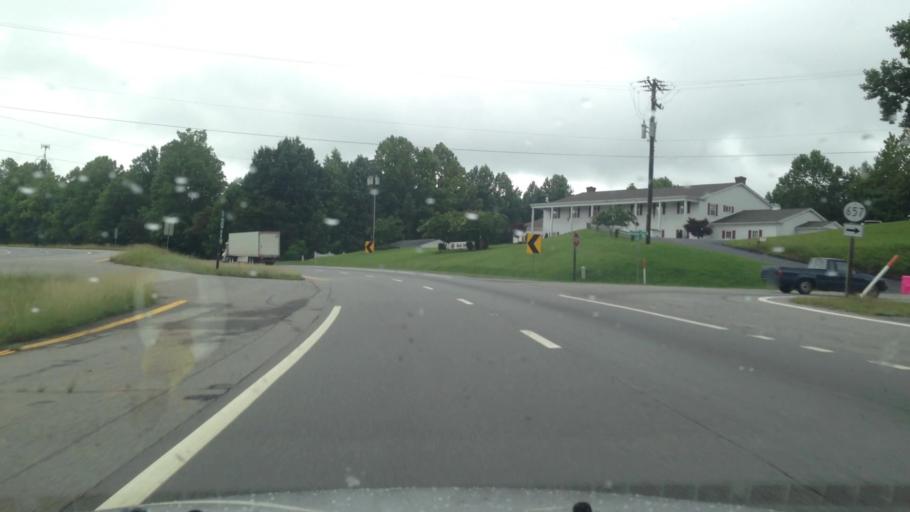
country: US
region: Virginia
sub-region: Henry County
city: Stanleytown
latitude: 36.7929
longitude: -79.9337
